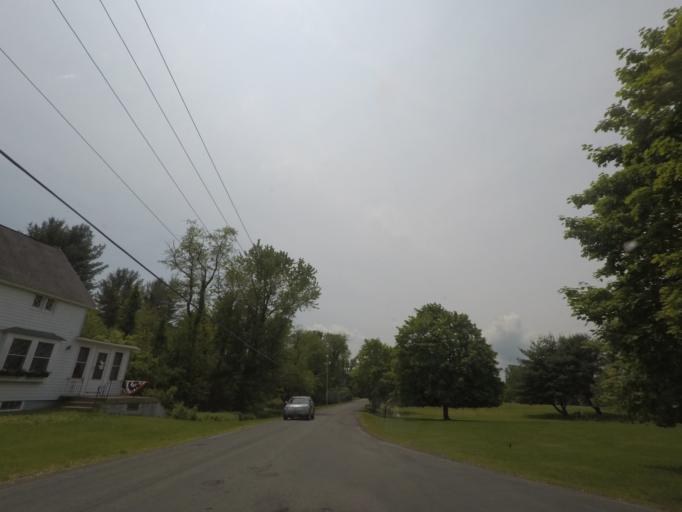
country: US
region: New York
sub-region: Rensselaer County
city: Castleton-on-Hudson
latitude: 42.5346
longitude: -73.7109
